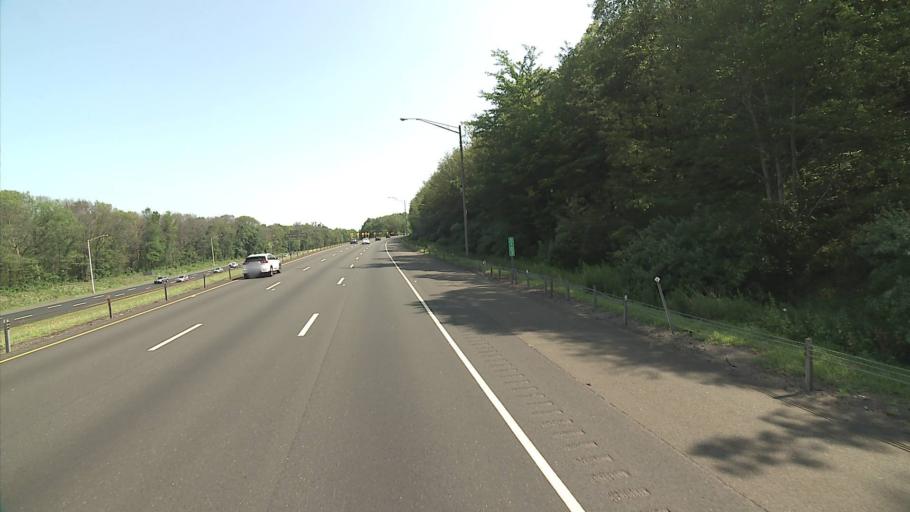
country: US
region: Connecticut
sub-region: New Haven County
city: Wallingford Center
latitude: 41.4160
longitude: -72.8291
